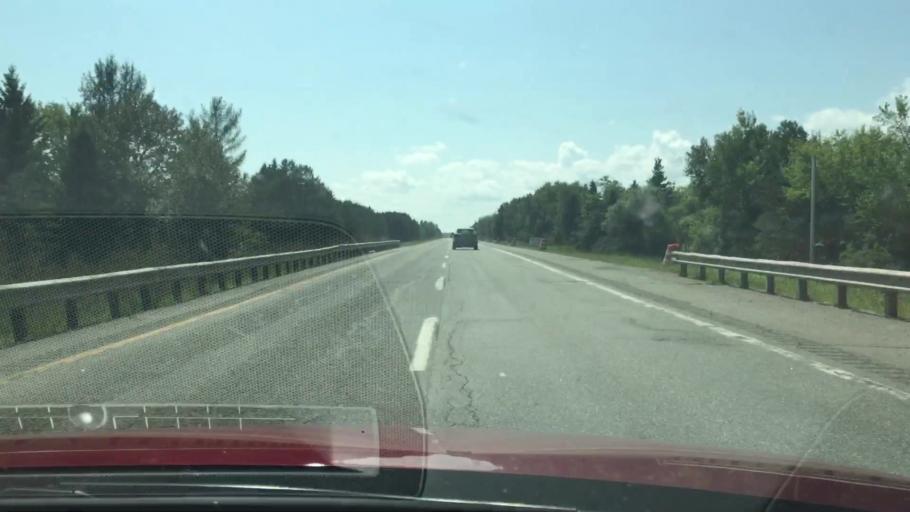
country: US
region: Maine
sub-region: Penobscot County
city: Patten
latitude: 45.8653
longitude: -68.4182
